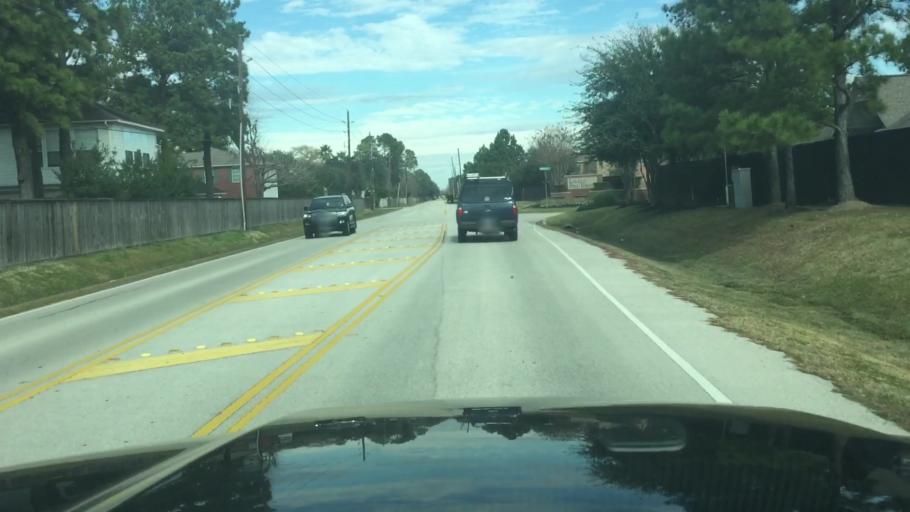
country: US
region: Texas
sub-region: Harris County
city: Oak Cliff Place
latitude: 29.8368
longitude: -95.6751
